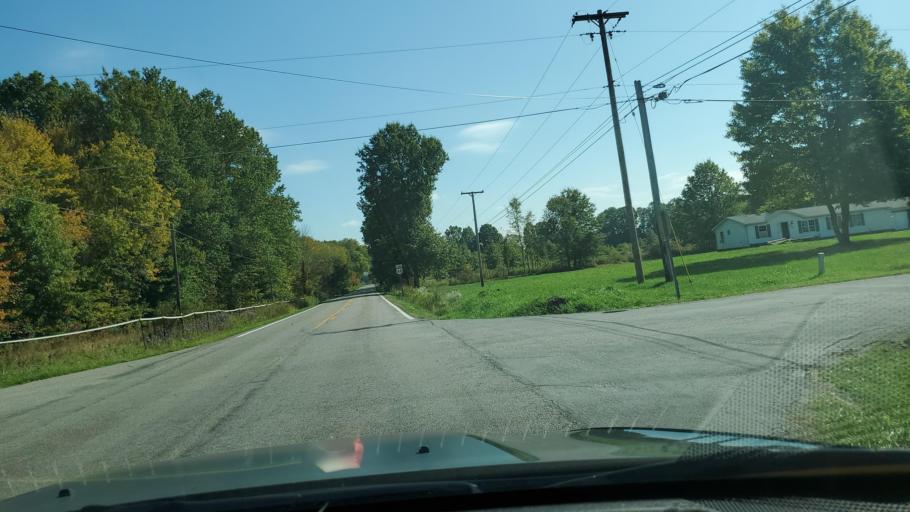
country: US
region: Ohio
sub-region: Trumbull County
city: Cortland
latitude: 41.3871
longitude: -80.5985
